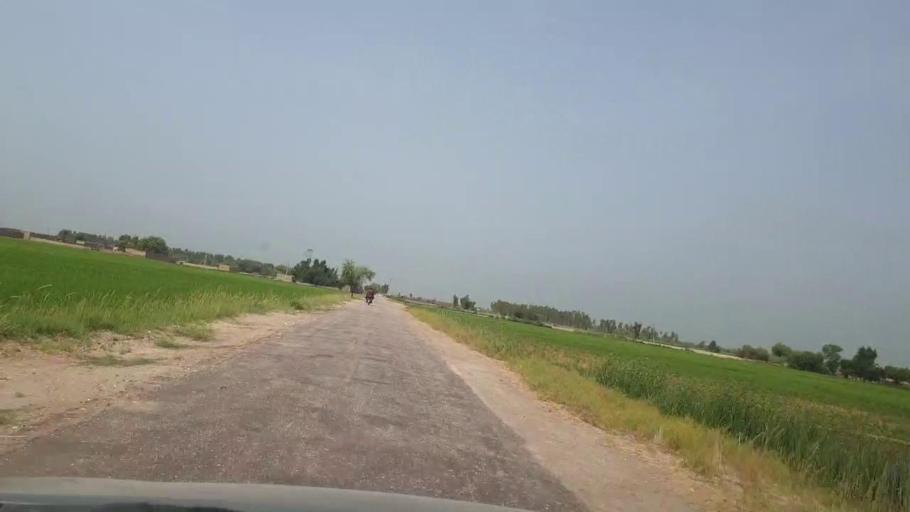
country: PK
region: Sindh
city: Garhi Yasin
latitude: 27.9197
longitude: 68.4401
